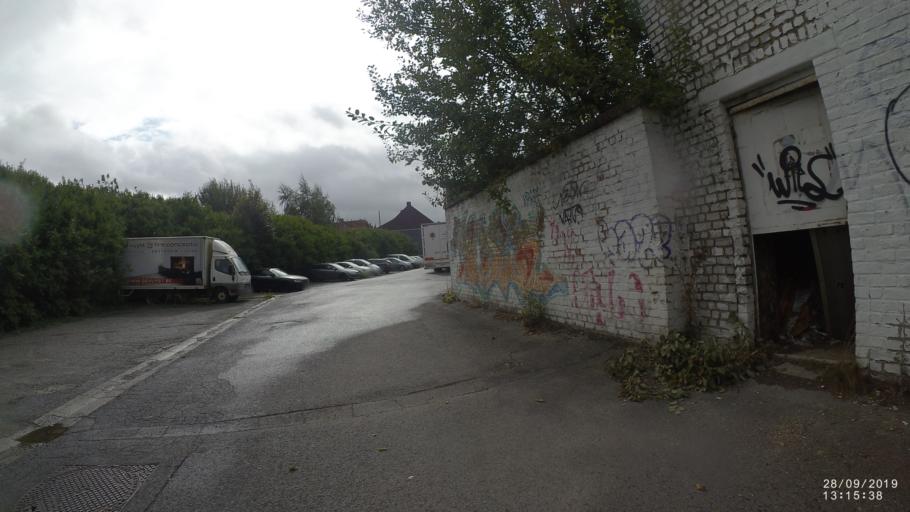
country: BE
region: Flanders
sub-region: Provincie Oost-Vlaanderen
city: Zottegem
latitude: 50.8737
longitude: 3.8131
